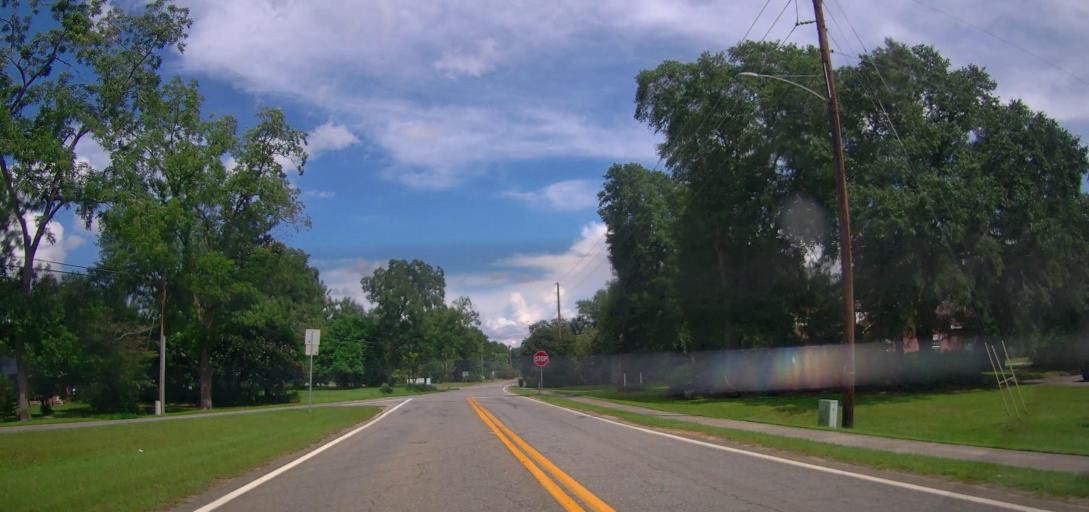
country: US
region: Georgia
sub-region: Taylor County
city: Butler
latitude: 32.5586
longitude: -84.2453
